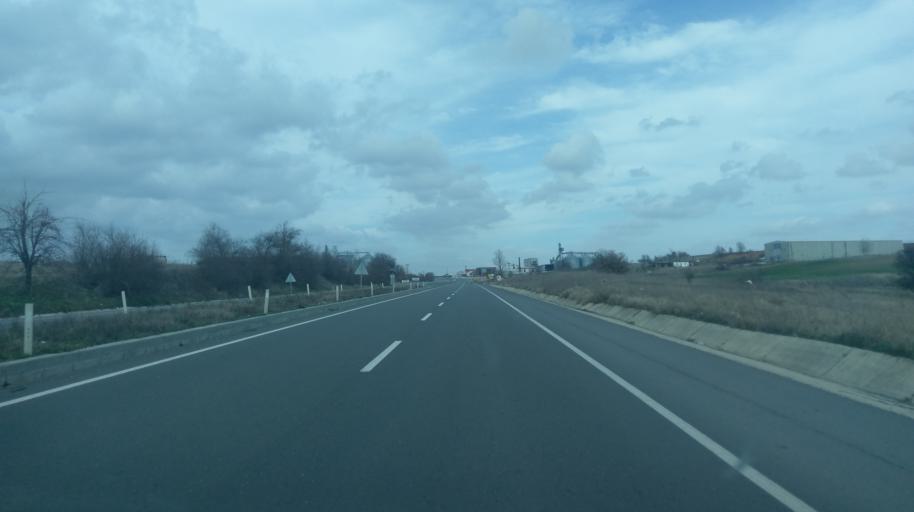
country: TR
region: Edirne
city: Hamidiye
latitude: 41.1992
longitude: 26.6737
